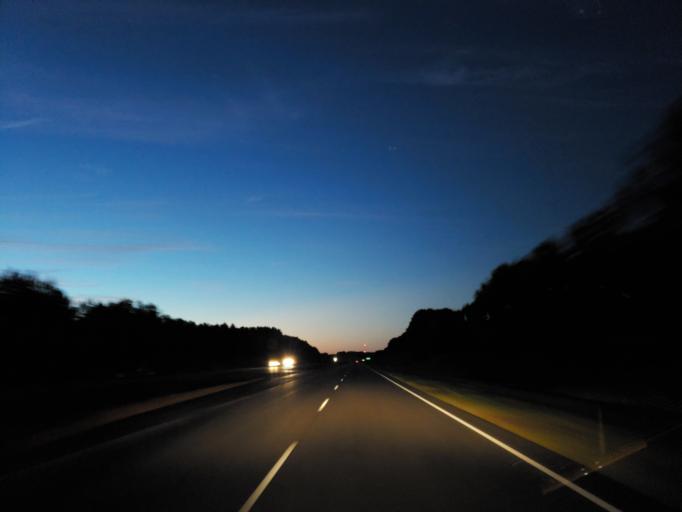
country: US
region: Mississippi
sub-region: Clarke County
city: Quitman
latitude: 32.0889
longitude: -88.6978
